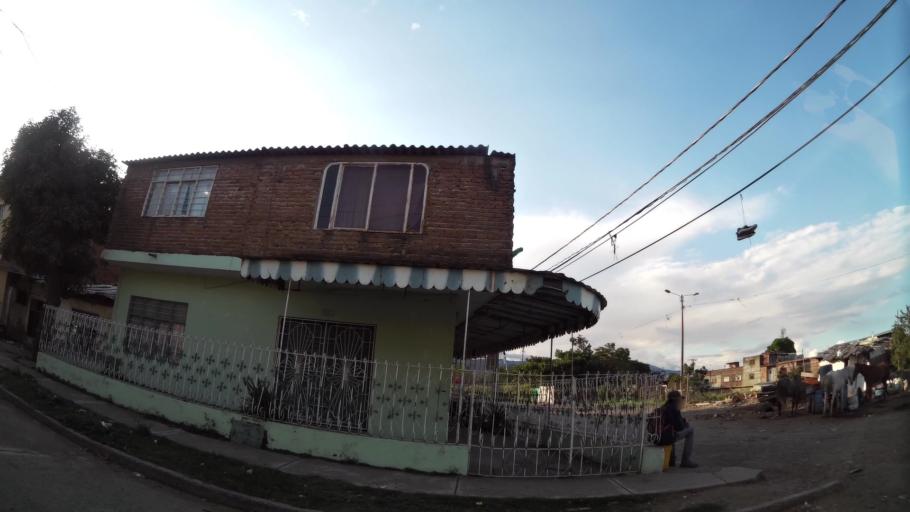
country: CO
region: Valle del Cauca
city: Cali
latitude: 3.4109
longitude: -76.5021
